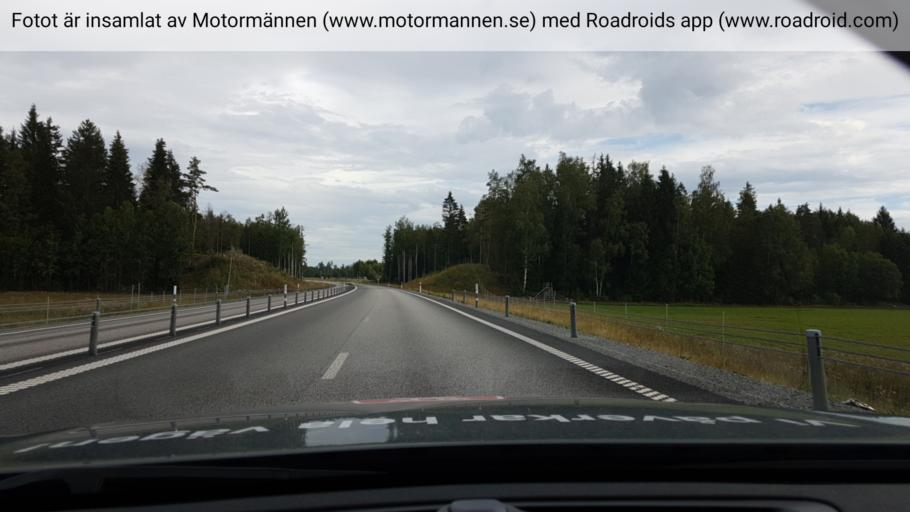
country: SE
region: Uppsala
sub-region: Heby Kommun
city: Heby
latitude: 60.0271
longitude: 16.8666
